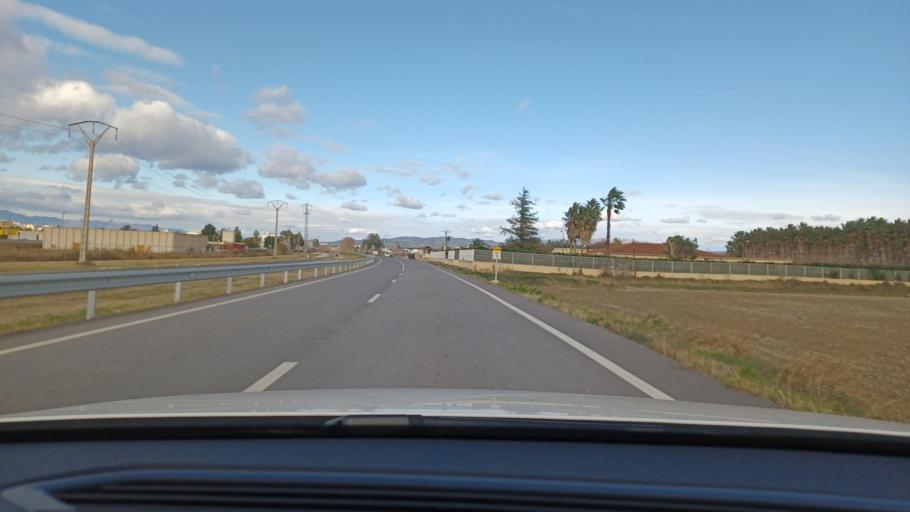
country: ES
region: Catalonia
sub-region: Provincia de Tarragona
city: Amposta
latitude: 40.6996
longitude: 0.5887
